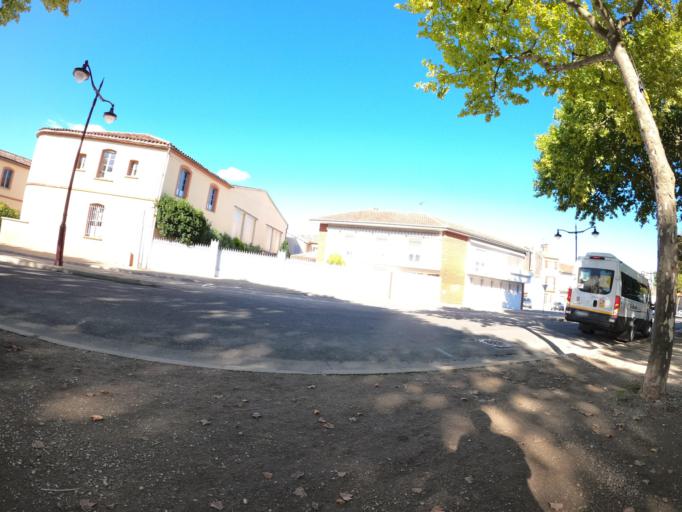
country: FR
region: Midi-Pyrenees
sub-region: Departement du Tarn-et-Garonne
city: Moissac
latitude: 44.1000
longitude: 1.0885
